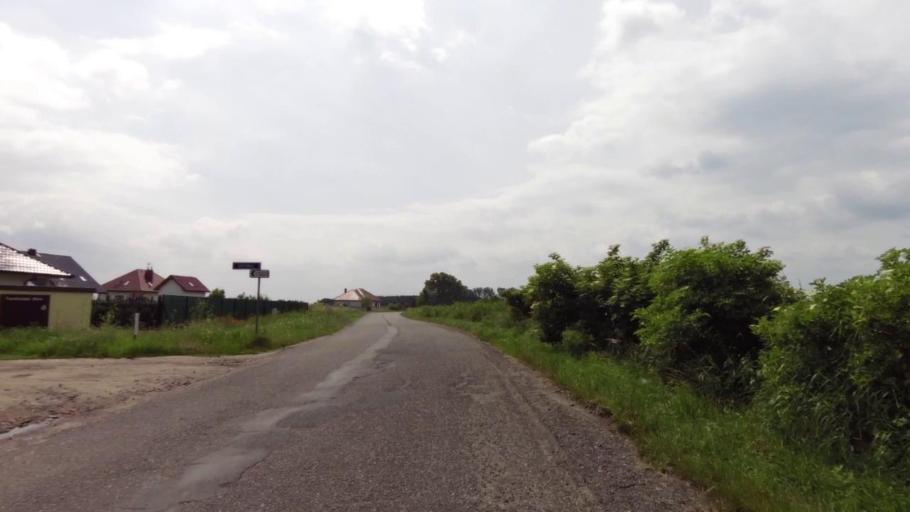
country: PL
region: West Pomeranian Voivodeship
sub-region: Powiat goleniowski
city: Goleniow
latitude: 53.5019
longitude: 14.7090
